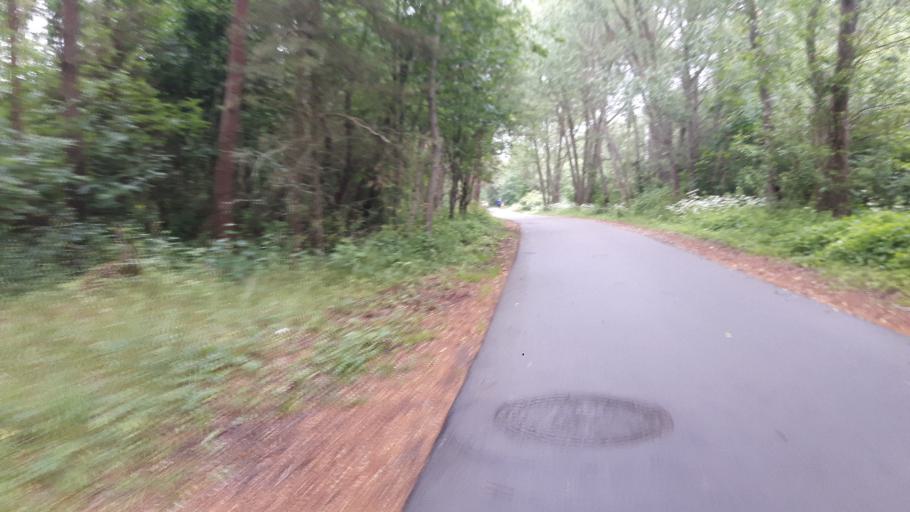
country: LT
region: Klaipedos apskritis
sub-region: Palanga
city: Sventoji
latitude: 56.0052
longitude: 21.0758
